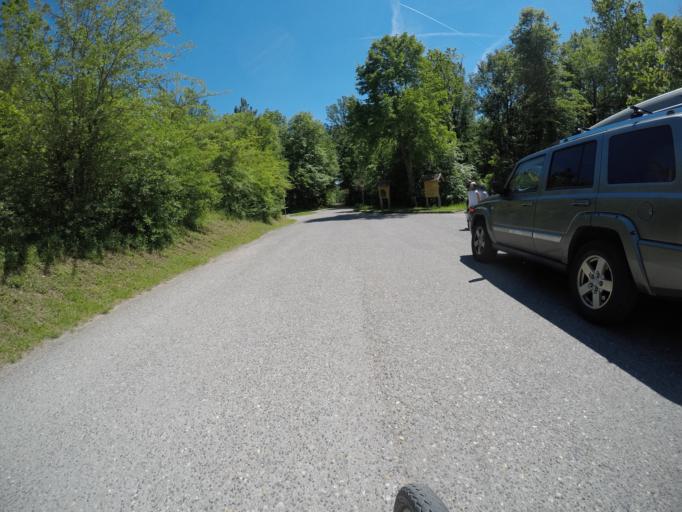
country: DE
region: Baden-Wuerttemberg
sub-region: Regierungsbezirk Stuttgart
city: Gerlingen
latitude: 48.7452
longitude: 9.0636
